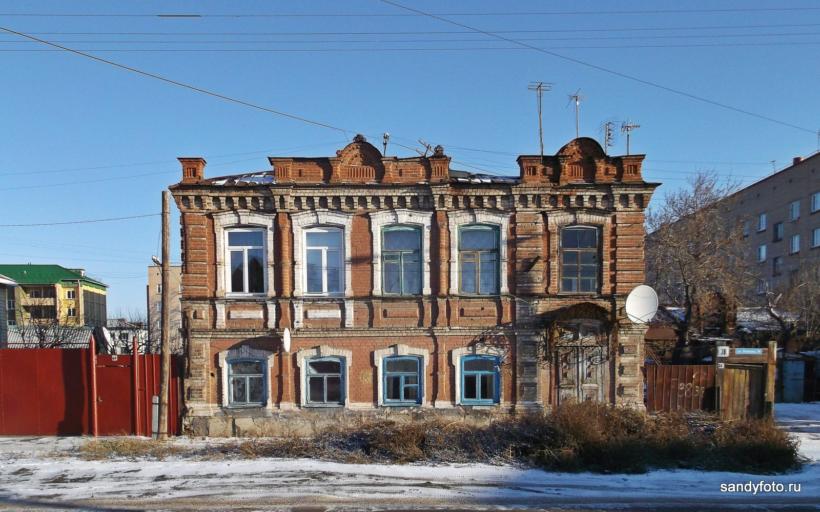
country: RU
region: Chelyabinsk
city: Troitsk
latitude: 54.0881
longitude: 61.5643
